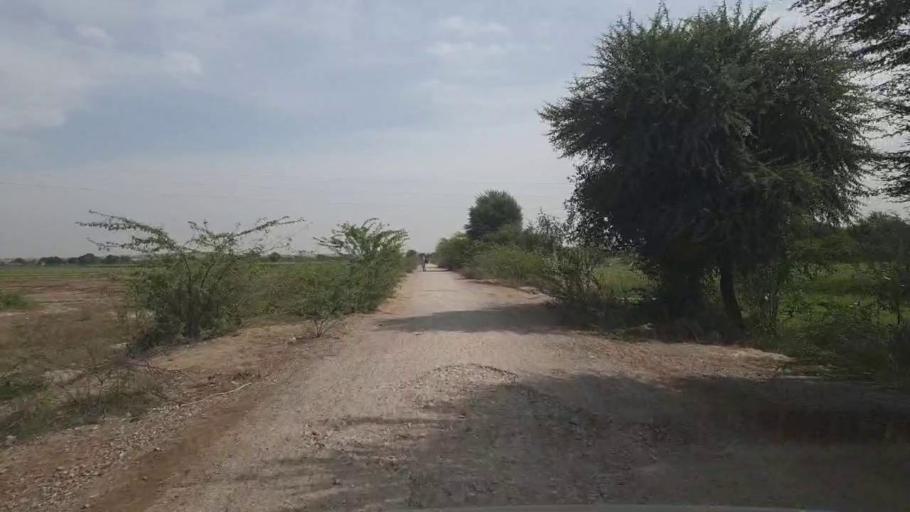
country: PK
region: Sindh
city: Kunri
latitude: 25.1983
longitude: 69.6810
